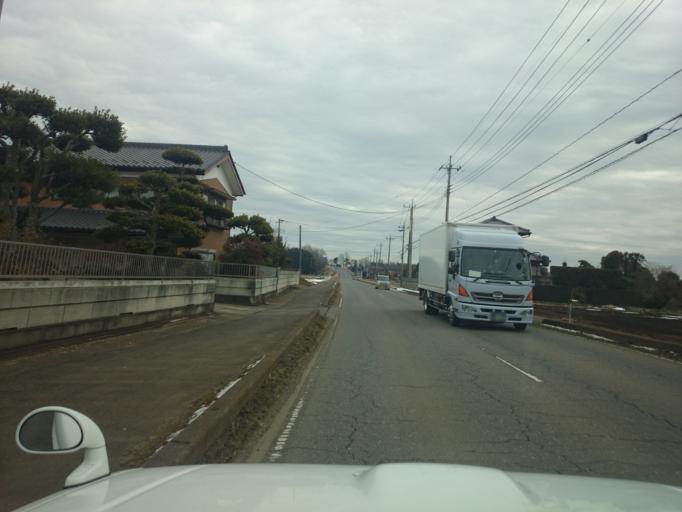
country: JP
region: Ibaraki
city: Tsukuba
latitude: 36.1108
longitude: 140.0678
